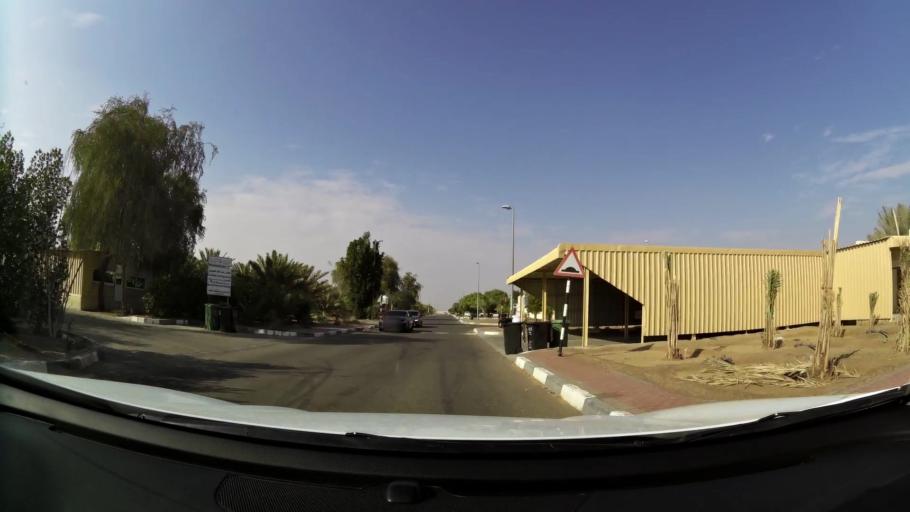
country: AE
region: Abu Dhabi
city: Al Ain
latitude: 24.0830
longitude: 55.8684
